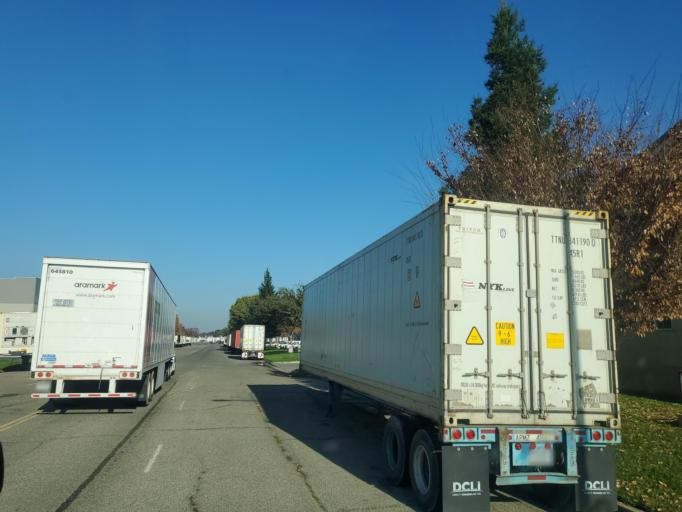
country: US
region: California
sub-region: San Joaquin County
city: French Camp
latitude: 37.8901
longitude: -121.2484
